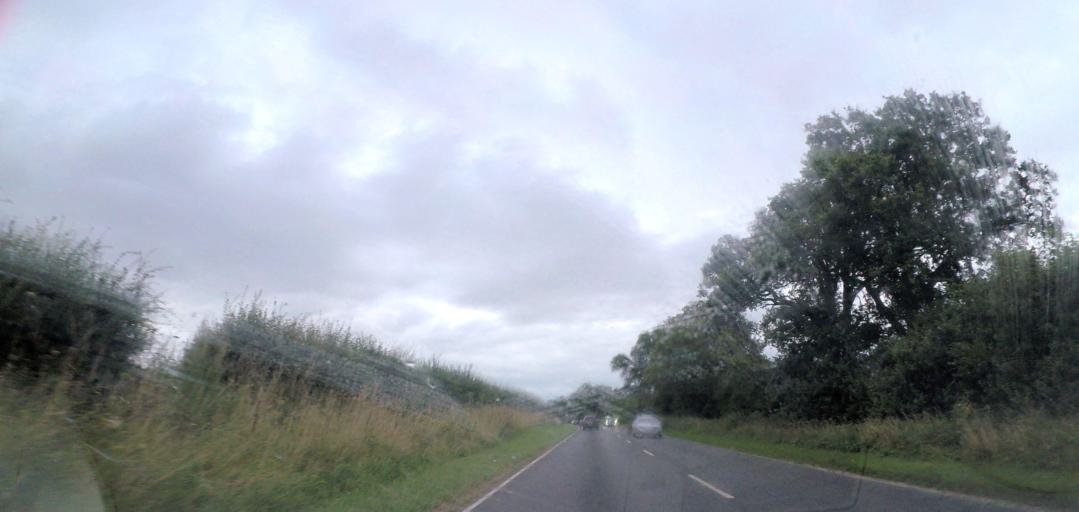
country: GB
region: England
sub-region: Norfolk
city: Coltishall
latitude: 52.7092
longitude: 1.3473
